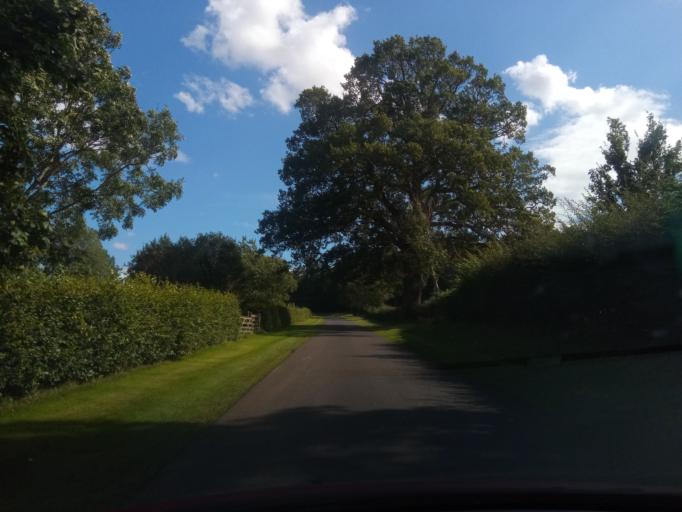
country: GB
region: Scotland
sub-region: The Scottish Borders
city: Coldstream
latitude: 55.6538
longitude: -2.2748
